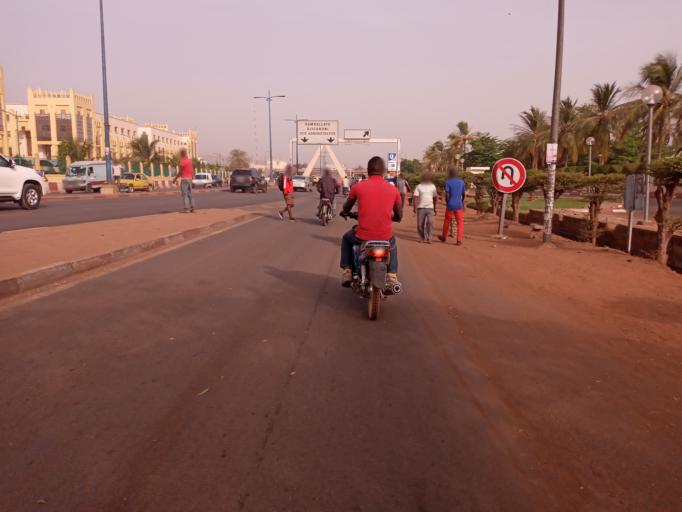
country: ML
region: Bamako
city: Bamako
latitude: 12.6297
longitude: -8.0091
